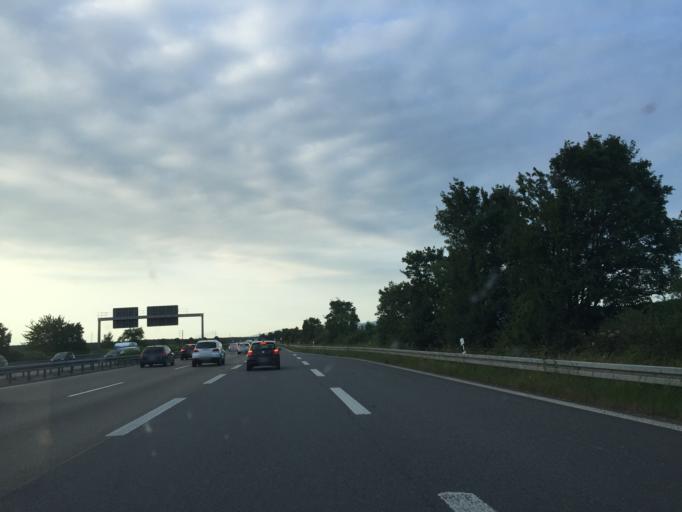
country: DE
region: Baden-Wuerttemberg
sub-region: Karlsruhe Region
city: Sankt Leon-Rot
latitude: 49.2868
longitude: 8.6232
